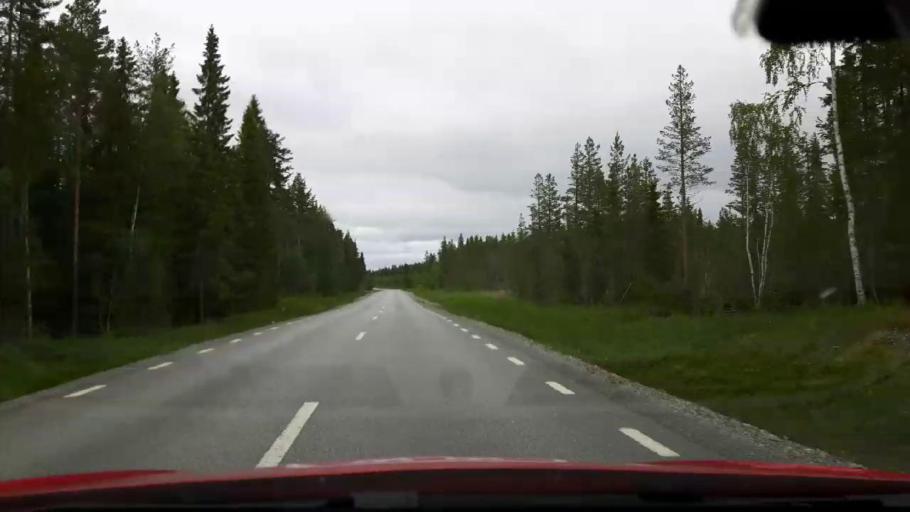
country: SE
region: Jaemtland
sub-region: OEstersunds Kommun
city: Lit
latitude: 63.7044
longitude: 14.6895
